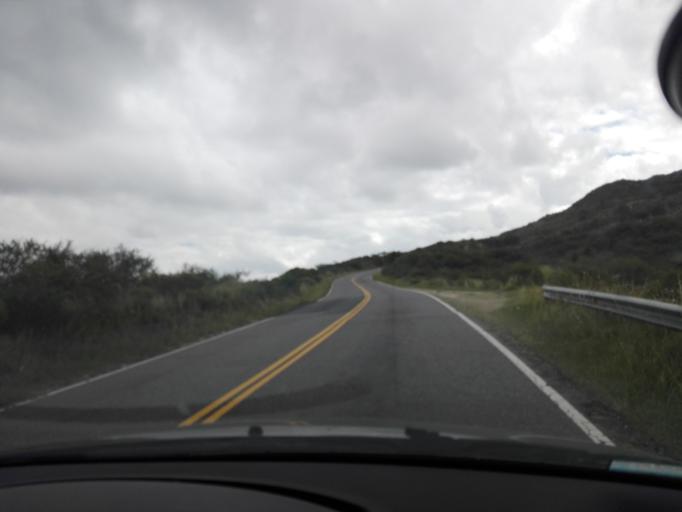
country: AR
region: Cordoba
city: Cuesta Blanca
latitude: -31.5932
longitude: -64.5277
